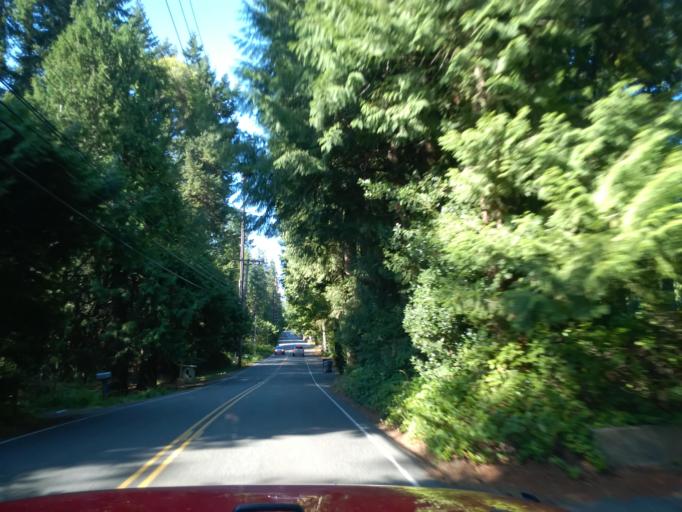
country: US
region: Washington
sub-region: King County
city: Sammamish
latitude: 47.6640
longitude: -122.0627
